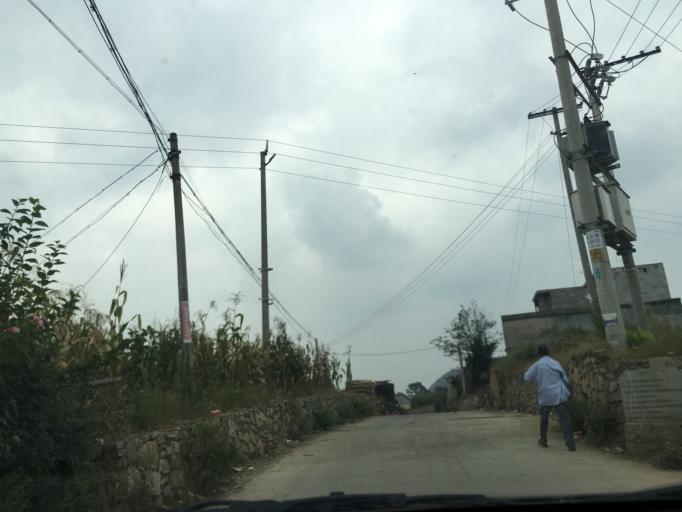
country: CN
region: Guangxi Zhuangzu Zizhiqu
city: Xinzhou
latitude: 25.5264
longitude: 105.6377
